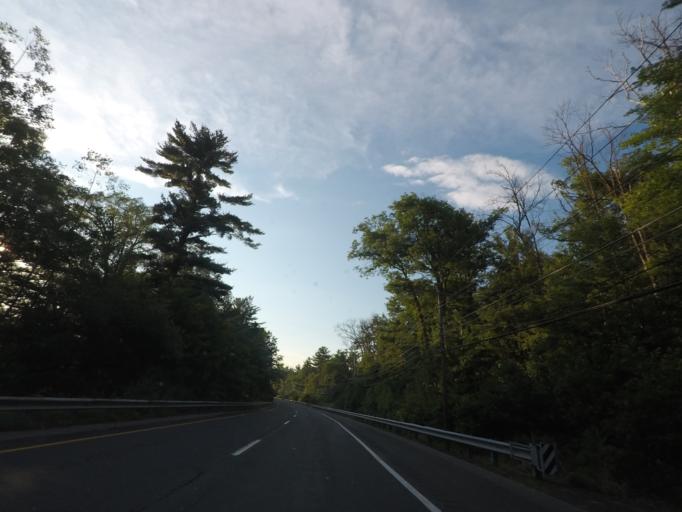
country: US
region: Massachusetts
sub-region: Hampden County
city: Brimfield
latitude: 42.1297
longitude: -72.2543
